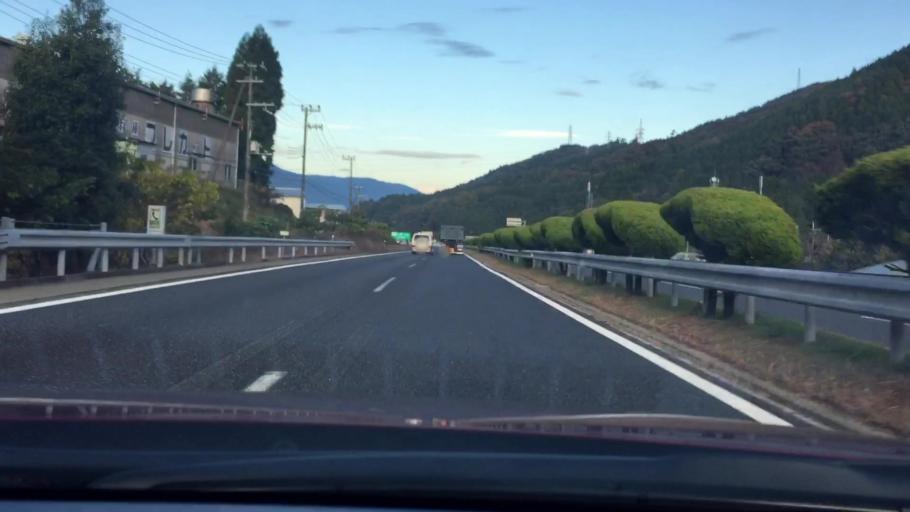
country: JP
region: Hyogo
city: Yamazakicho-nakabirose
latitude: 34.9927
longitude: 134.5740
